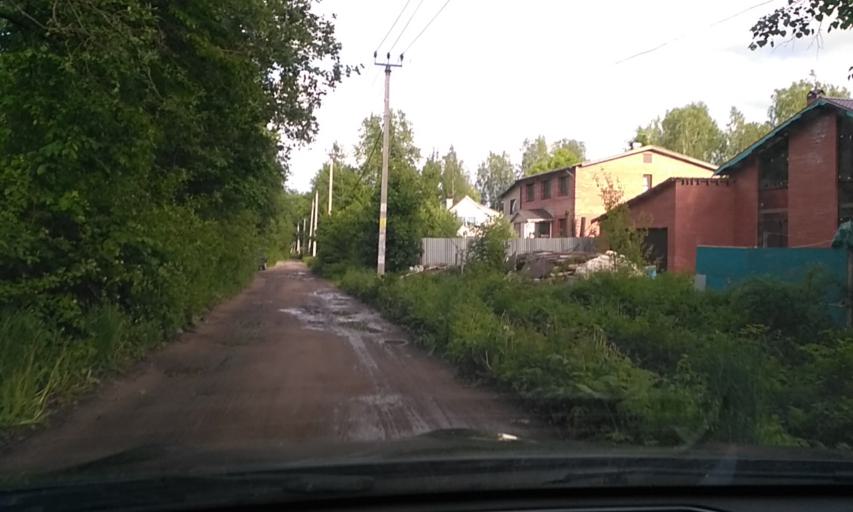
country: RU
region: Leningrad
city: Otradnoye
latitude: 59.8070
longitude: 30.8118
